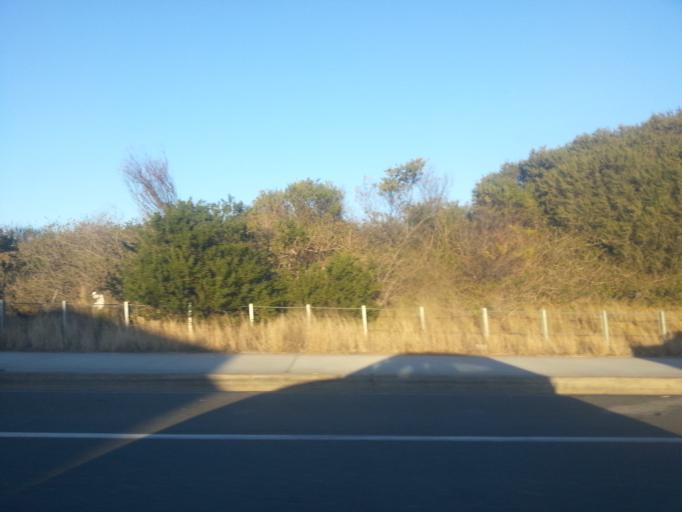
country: AU
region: New South Wales
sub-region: Wollongong
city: Port Kembla
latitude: -34.4920
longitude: 150.8935
